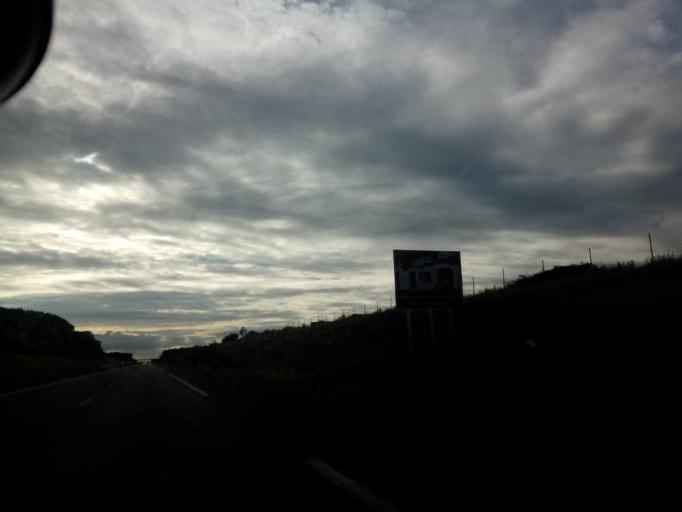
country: FR
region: Centre
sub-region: Departement d'Indre-et-Loire
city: Monts
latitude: 47.3068
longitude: 0.6304
